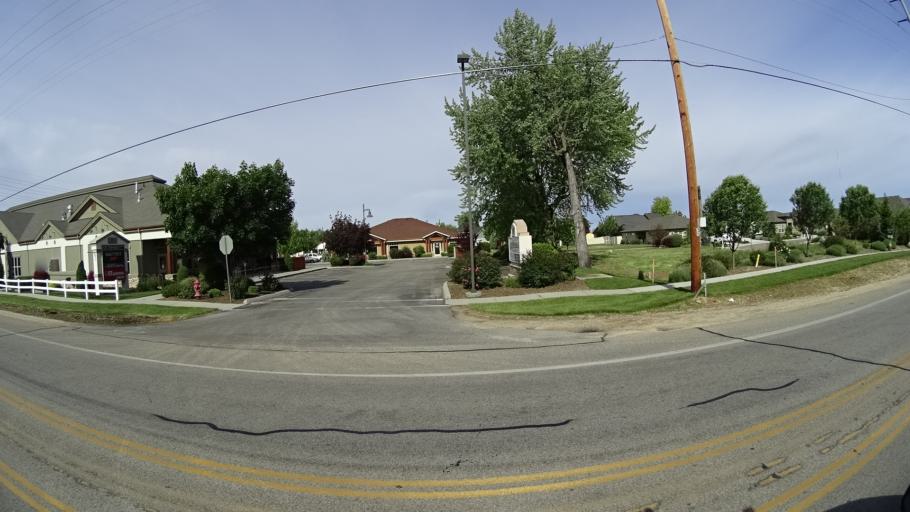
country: US
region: Idaho
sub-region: Ada County
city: Meridian
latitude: 43.5618
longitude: -116.3344
